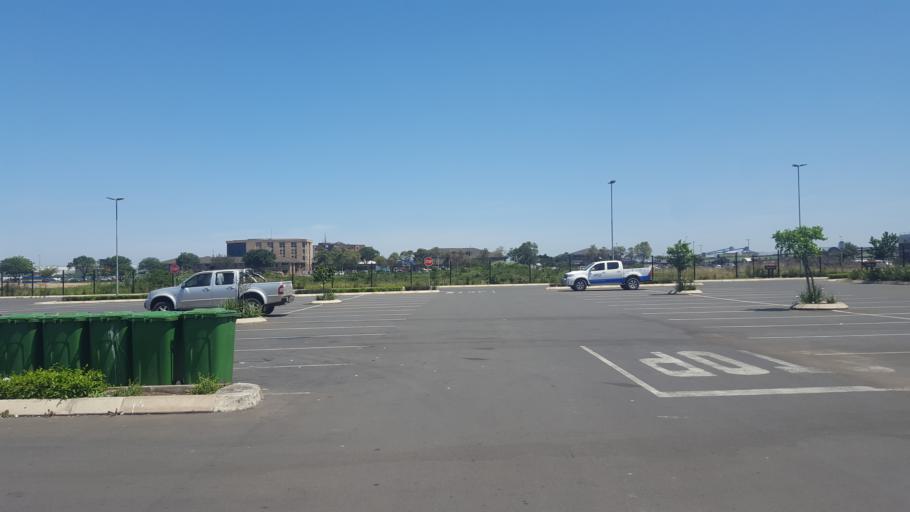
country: ZA
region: KwaZulu-Natal
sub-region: uThungulu District Municipality
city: Richards Bay
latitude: -28.7474
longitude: 32.0507
